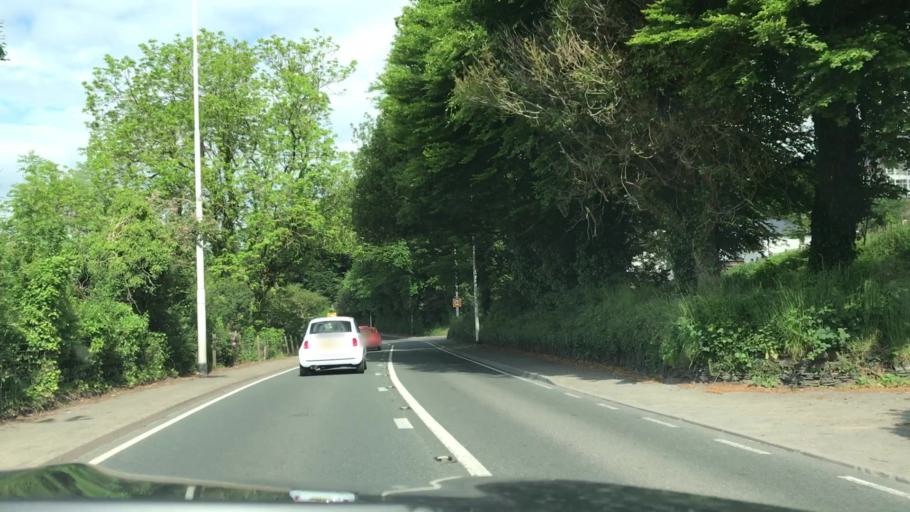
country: GB
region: Wales
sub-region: County of Ceredigion
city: Penparcau
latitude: 52.4055
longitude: -4.0526
